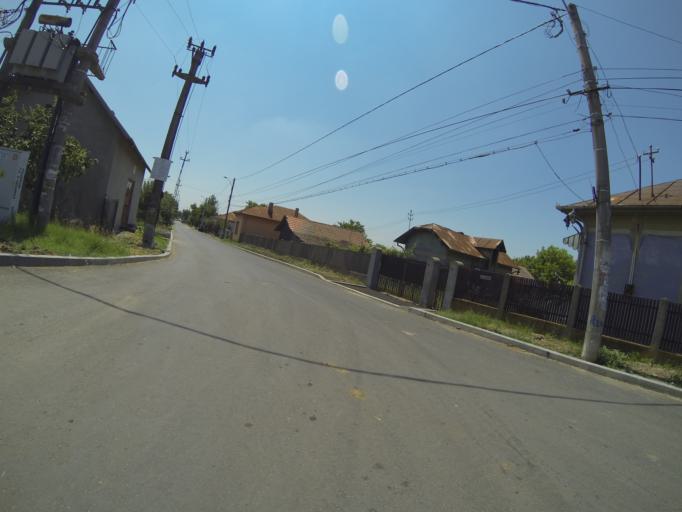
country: RO
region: Dolj
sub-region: Comuna Segarcea
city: Segarcea
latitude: 44.0939
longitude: 23.7516
